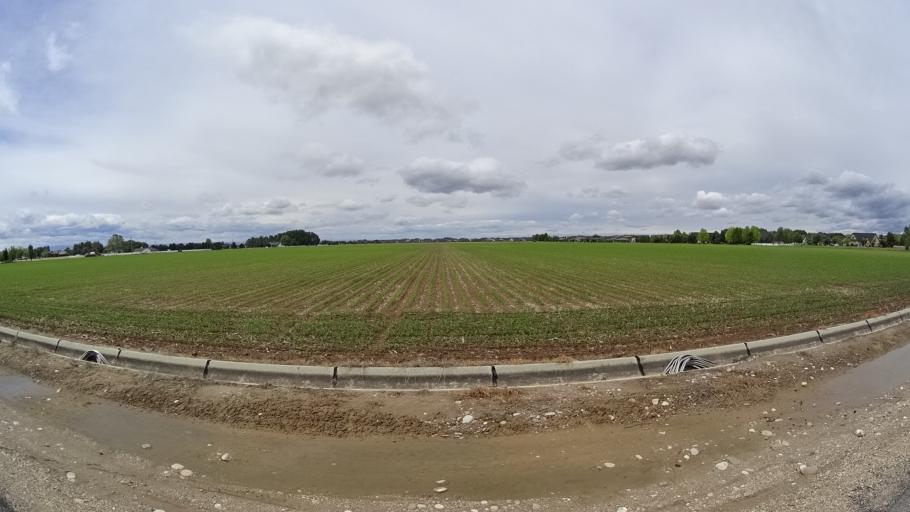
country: US
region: Idaho
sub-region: Ada County
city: Eagle
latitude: 43.7082
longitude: -116.4035
